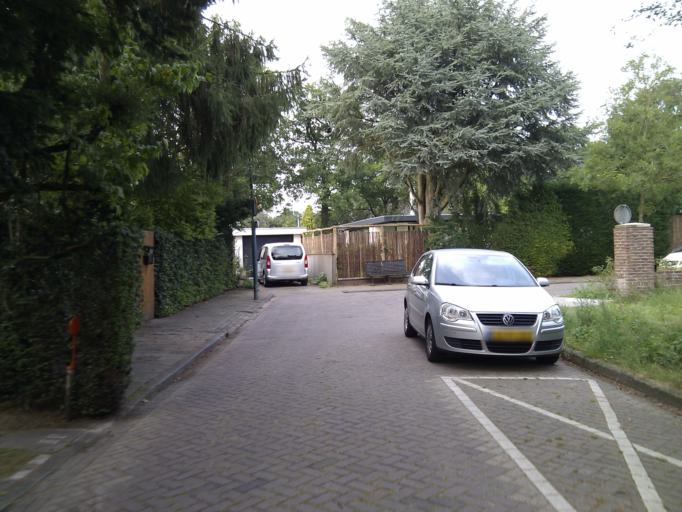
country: NL
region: Utrecht
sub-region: Gemeente De Bilt
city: De Bilt
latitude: 52.1124
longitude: 5.1880
